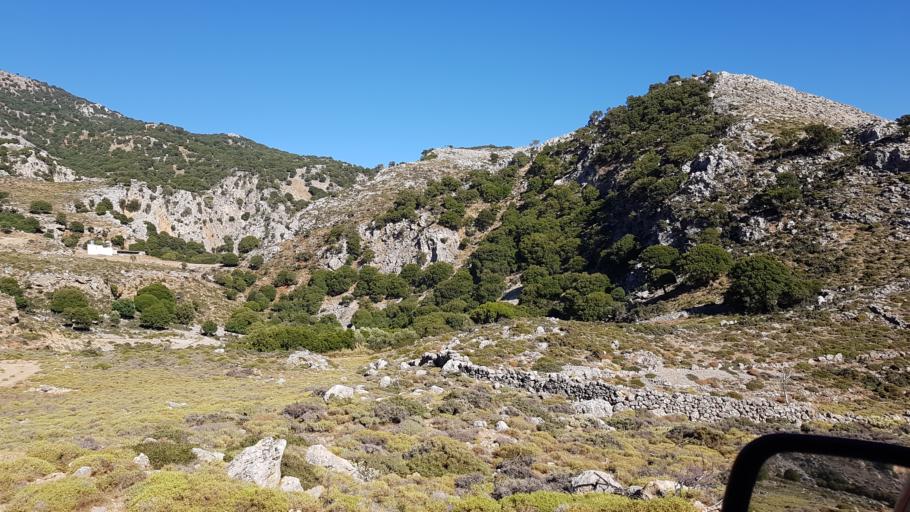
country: GR
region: Crete
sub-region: Nomos Rethymnis
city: Agia Galini
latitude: 35.1929
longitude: 24.7464
